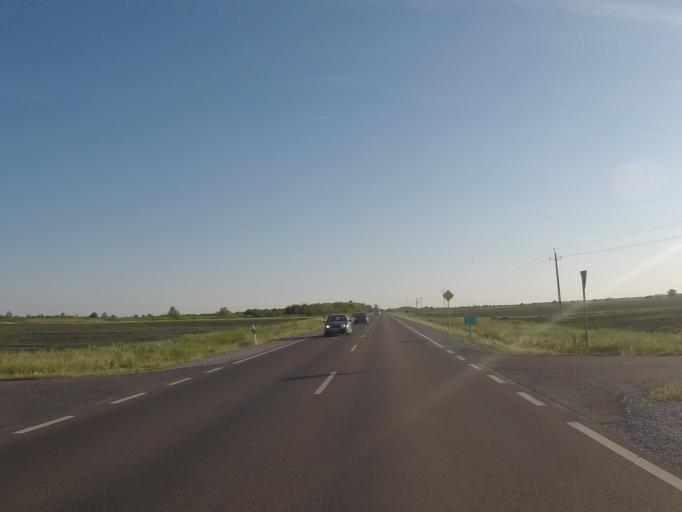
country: HU
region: Heves
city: Erdotelek
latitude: 47.6755
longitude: 20.3729
